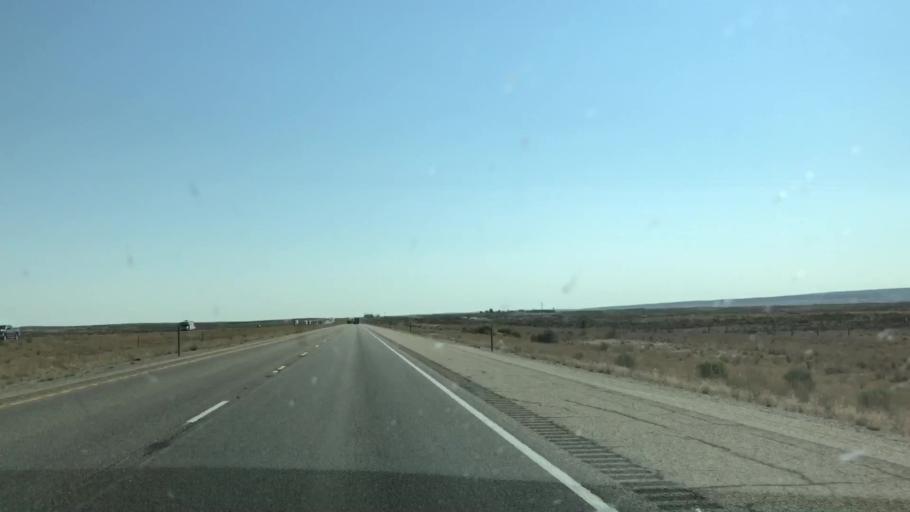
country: US
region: Wyoming
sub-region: Sweetwater County
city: Rock Springs
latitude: 41.6366
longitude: -108.4364
